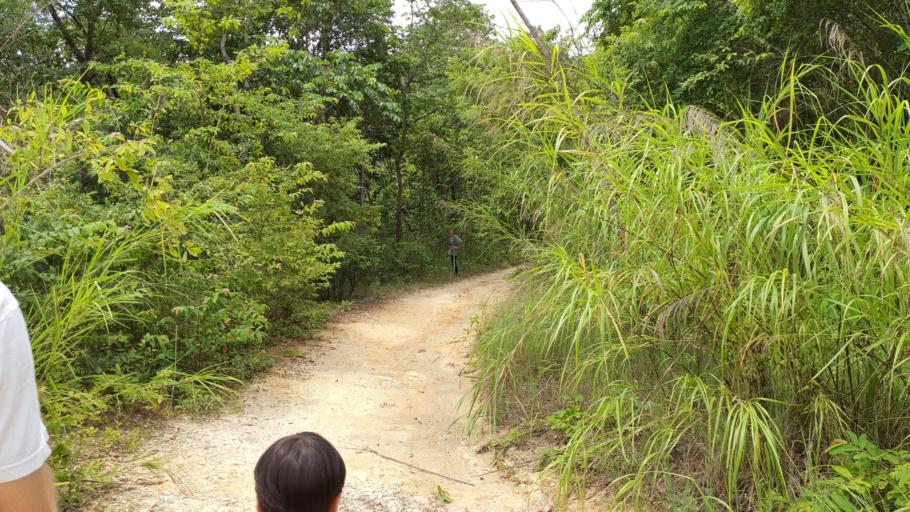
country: TH
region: Chiang Mai
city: Chiang Mai
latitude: 18.7696
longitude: 98.9103
